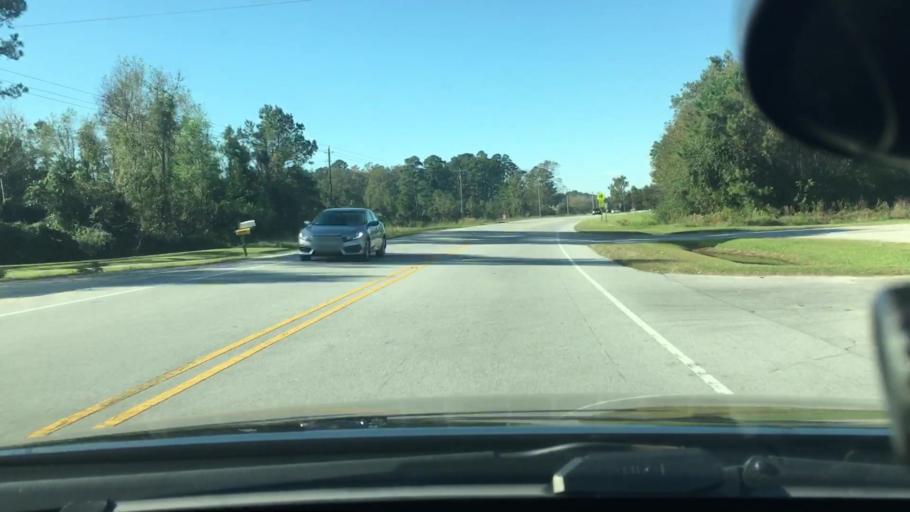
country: US
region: North Carolina
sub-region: Craven County
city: Trent Woods
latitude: 35.1604
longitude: -77.1174
